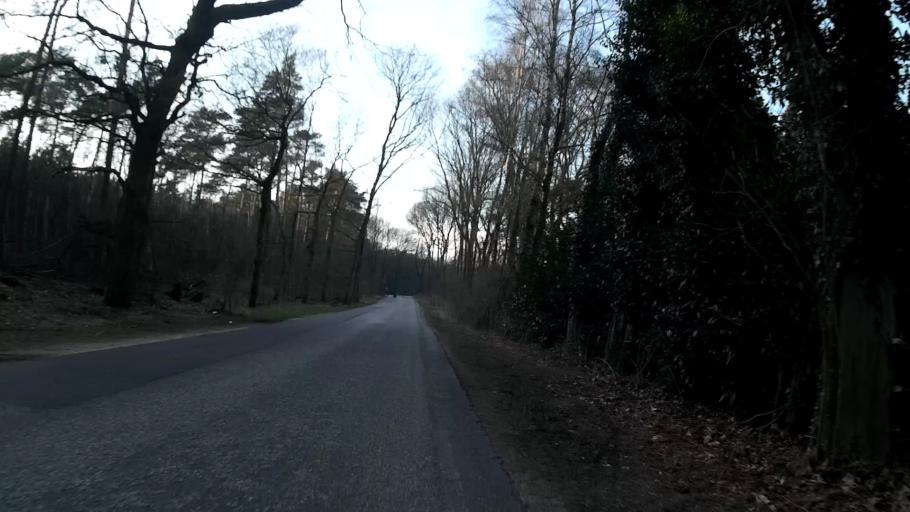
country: NL
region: Utrecht
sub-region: Gemeente Veenendaal
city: Veenendaal
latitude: 51.9969
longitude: 5.5469
